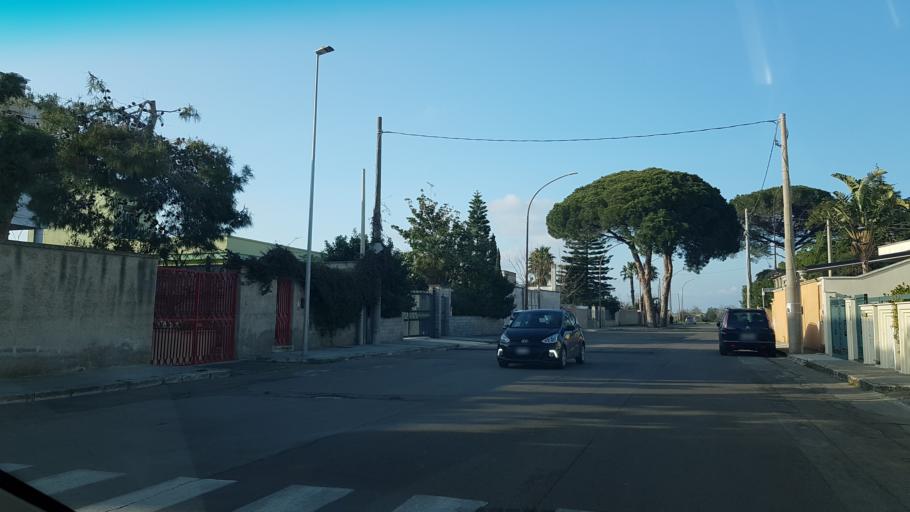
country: IT
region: Apulia
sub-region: Provincia di Lecce
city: Trepuzzi
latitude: 40.4111
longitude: 18.0704
